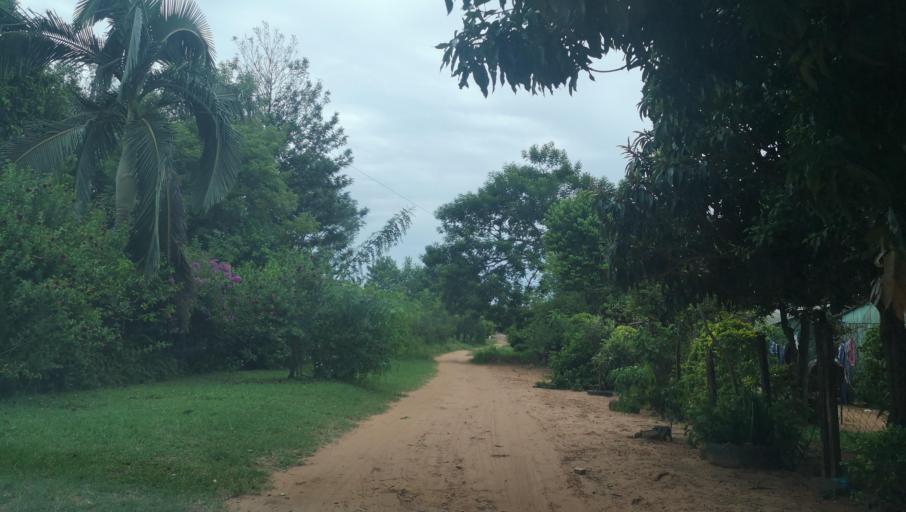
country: PY
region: San Pedro
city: Capiibary
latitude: -24.7386
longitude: -56.0211
